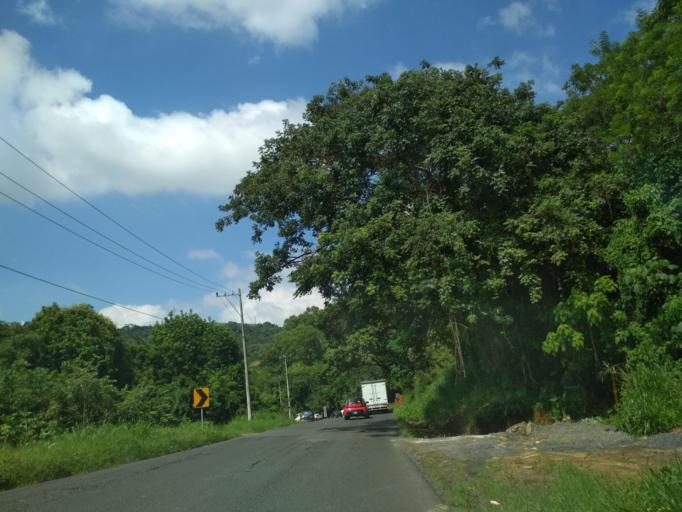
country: MX
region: Veracruz
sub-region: San Andres Tuxtla
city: Texcaltitan Xoteapan (Texcaltitan)
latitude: 18.4401
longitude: -95.2582
